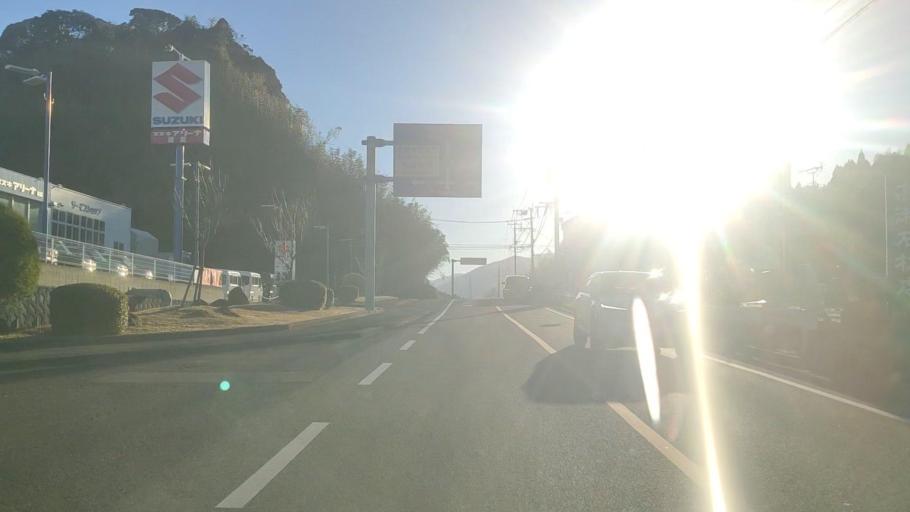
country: JP
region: Miyazaki
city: Miyazaki-shi
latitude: 31.8653
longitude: 131.3893
